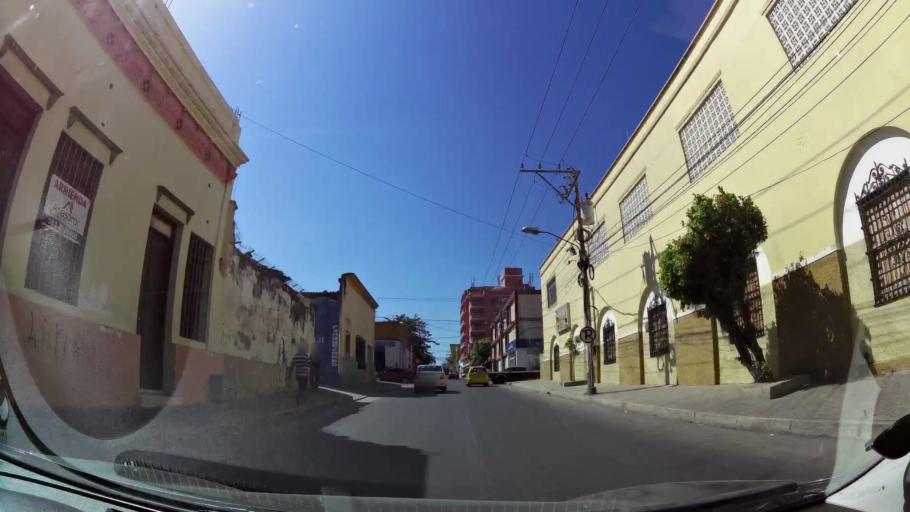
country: CO
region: Atlantico
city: Barranquilla
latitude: 10.9857
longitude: -74.7823
